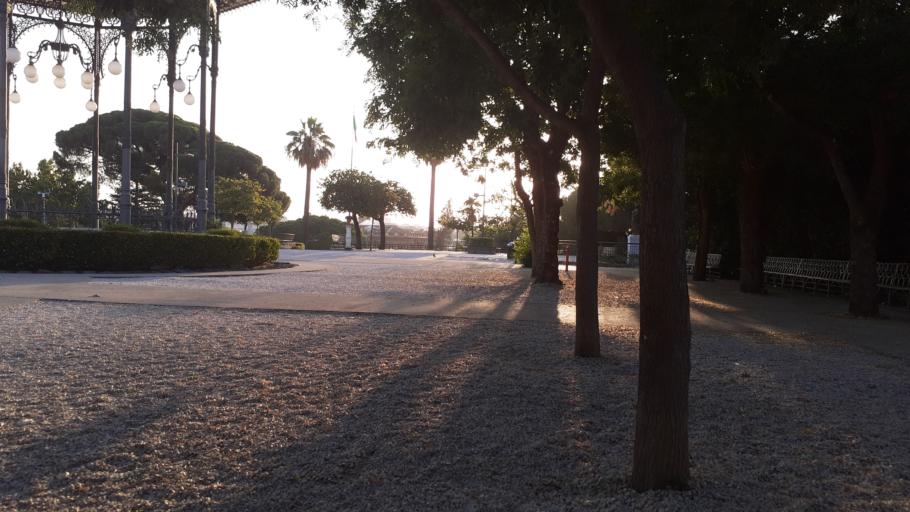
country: IT
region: Sicily
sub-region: Catania
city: Catania
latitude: 37.5102
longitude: 15.0833
